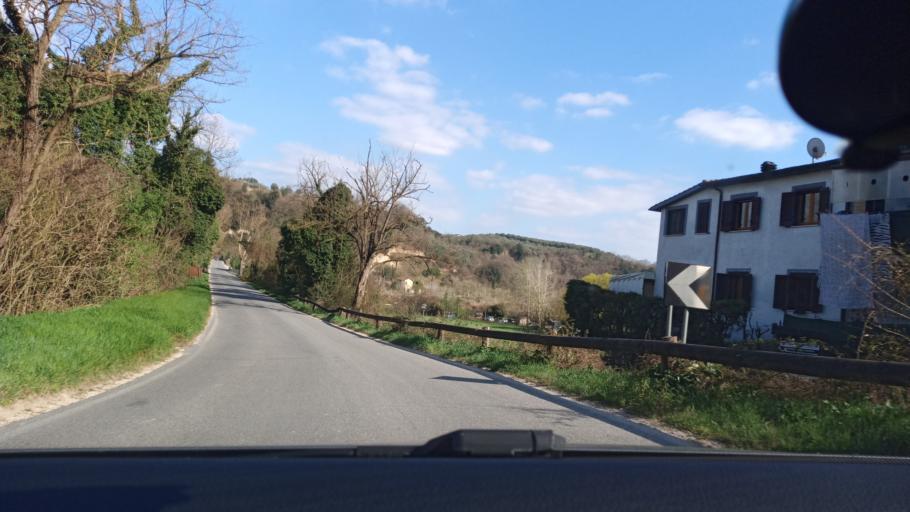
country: IT
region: Latium
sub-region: Citta metropolitana di Roma Capitale
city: Torrita Tiberina
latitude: 42.2357
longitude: 12.6271
